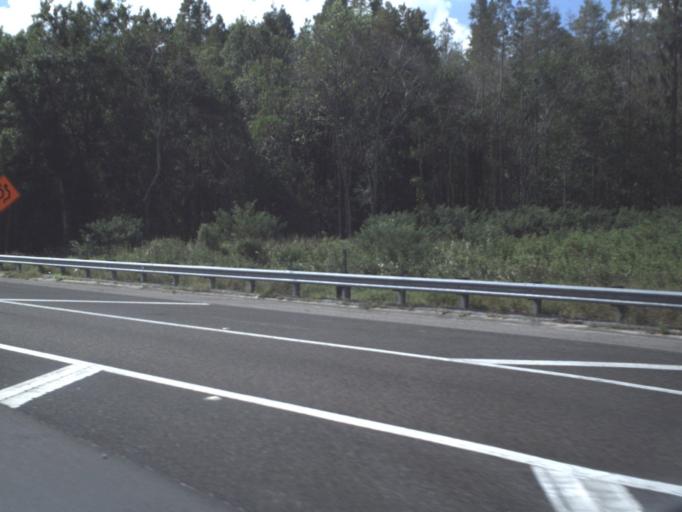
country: US
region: Florida
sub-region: Hillsborough County
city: Greater Northdale
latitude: 28.1175
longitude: -82.5461
